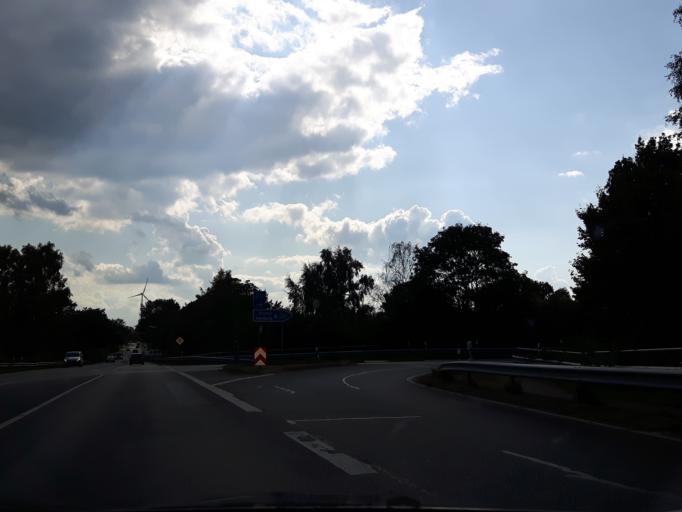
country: DE
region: Lower Saxony
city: Hatten
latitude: 53.0620
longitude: 8.3536
